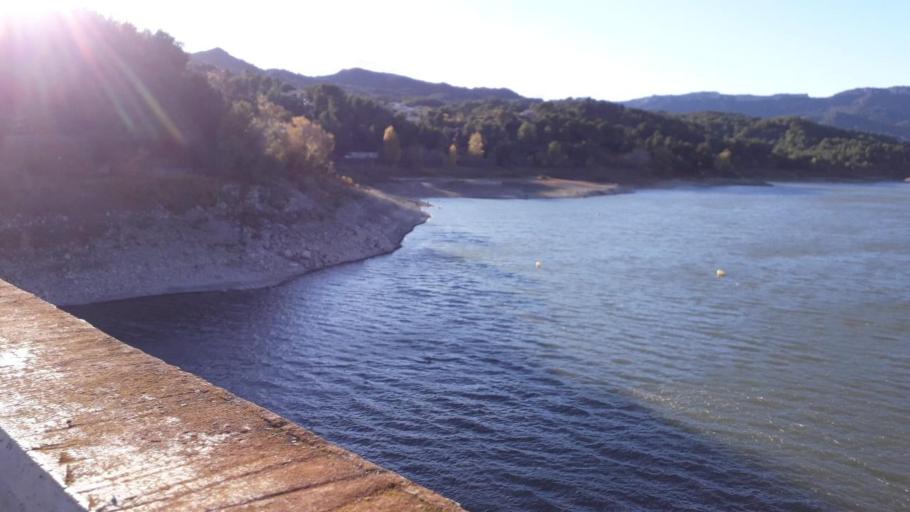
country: ES
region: Catalonia
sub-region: Provincia de Tarragona
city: Riudecanyes
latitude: 41.1336
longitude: 0.9586
